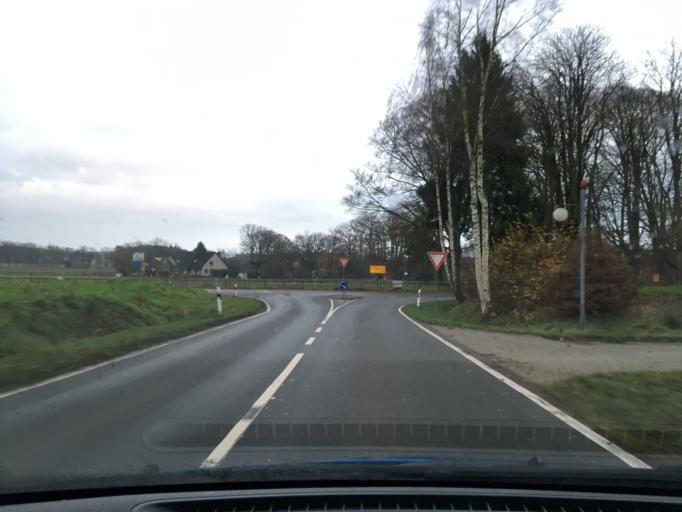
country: DE
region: Lower Saxony
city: Hermannsburg
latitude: 52.8180
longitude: 10.0592
